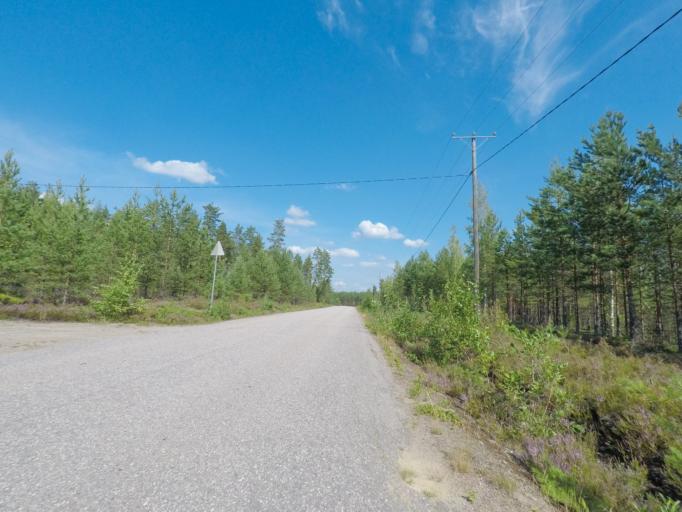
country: FI
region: Southern Savonia
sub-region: Mikkeli
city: Puumala
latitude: 61.4286
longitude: 28.1651
